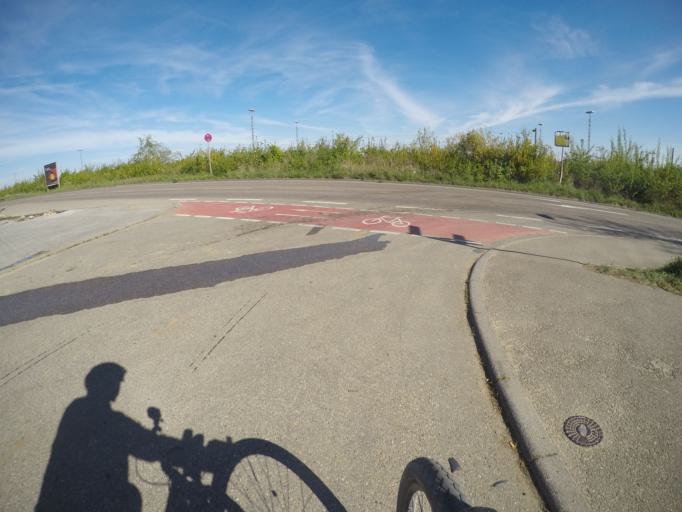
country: DE
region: Baden-Wuerttemberg
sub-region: Regierungsbezirk Stuttgart
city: Kornwestheim
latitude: 48.8679
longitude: 9.1740
